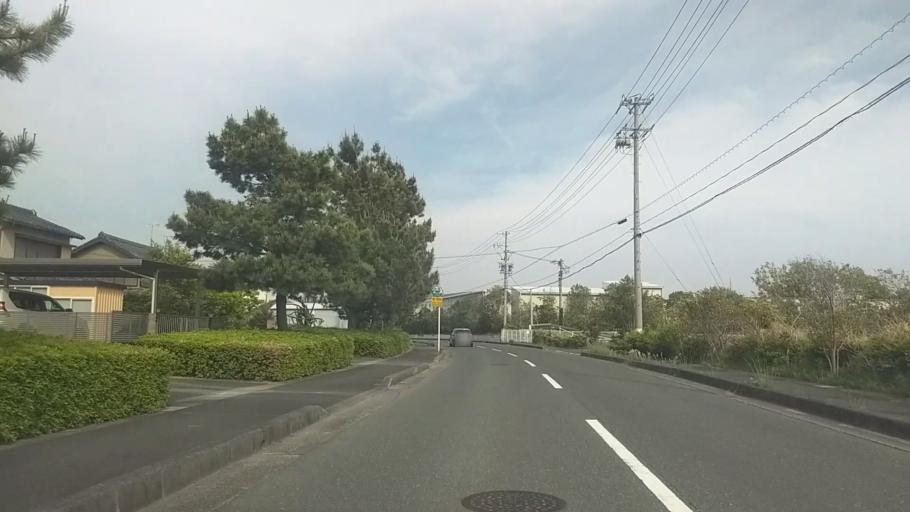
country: JP
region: Shizuoka
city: Kosai-shi
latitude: 34.7212
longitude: 137.5943
